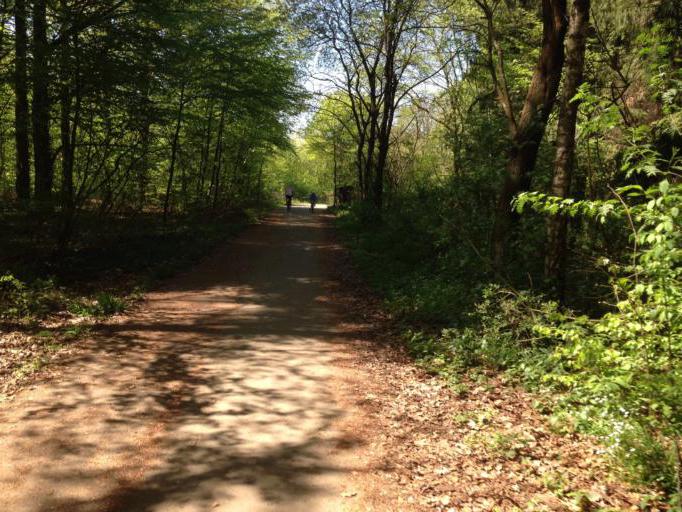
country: DE
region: Hesse
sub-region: Regierungsbezirk Giessen
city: Giessen
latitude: 50.5595
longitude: 8.6636
